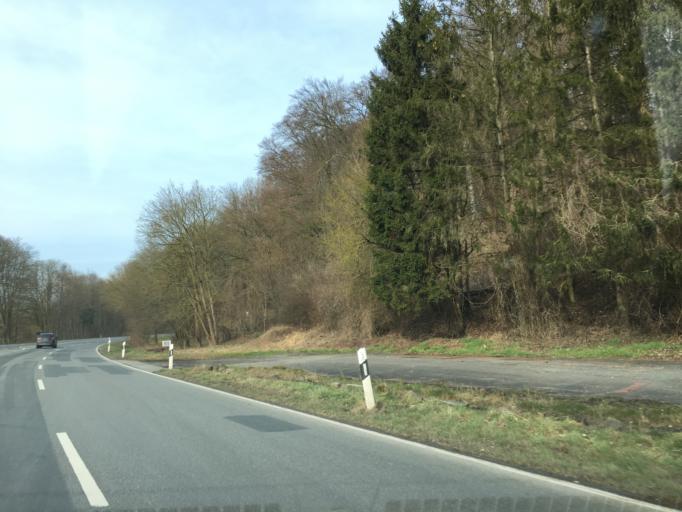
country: DE
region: North Rhine-Westphalia
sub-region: Regierungsbezirk Detmold
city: Willebadessen
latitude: 51.5392
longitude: 9.0148
